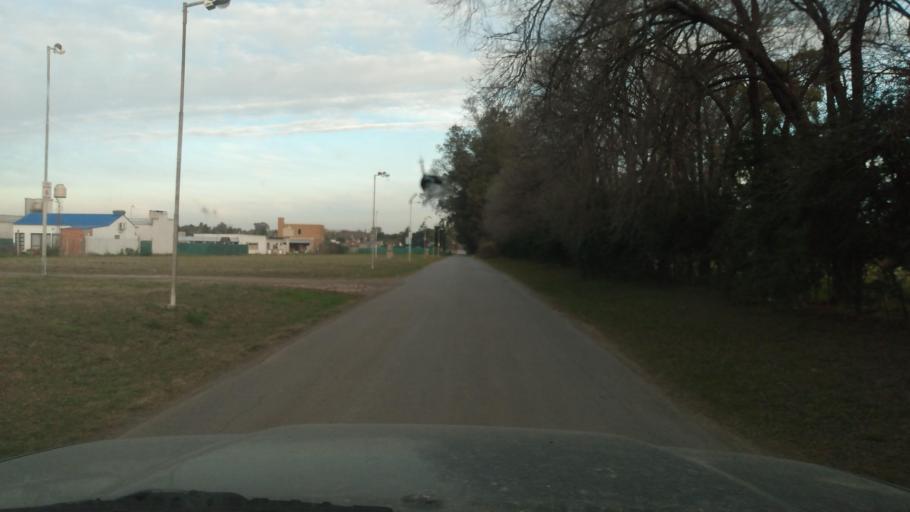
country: AR
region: Buenos Aires
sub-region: Partido de Lujan
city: Lujan
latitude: -34.5740
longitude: -59.0711
